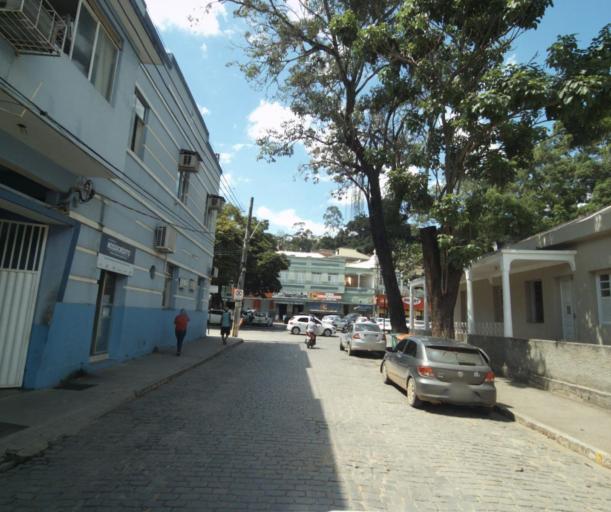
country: BR
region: Espirito Santo
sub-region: Mimoso Do Sul
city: Mimoso do Sul
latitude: -21.0631
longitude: -41.3636
